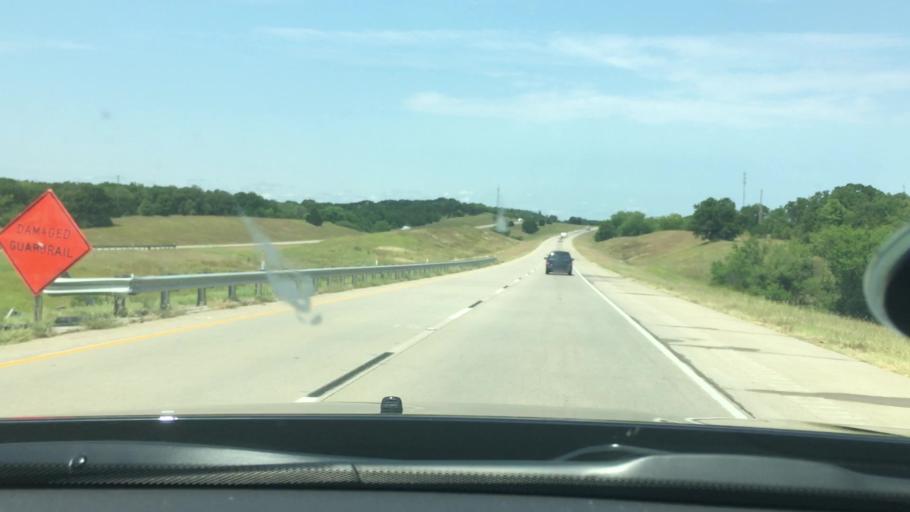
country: US
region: Oklahoma
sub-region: Love County
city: Marietta
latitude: 33.9859
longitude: -97.1367
